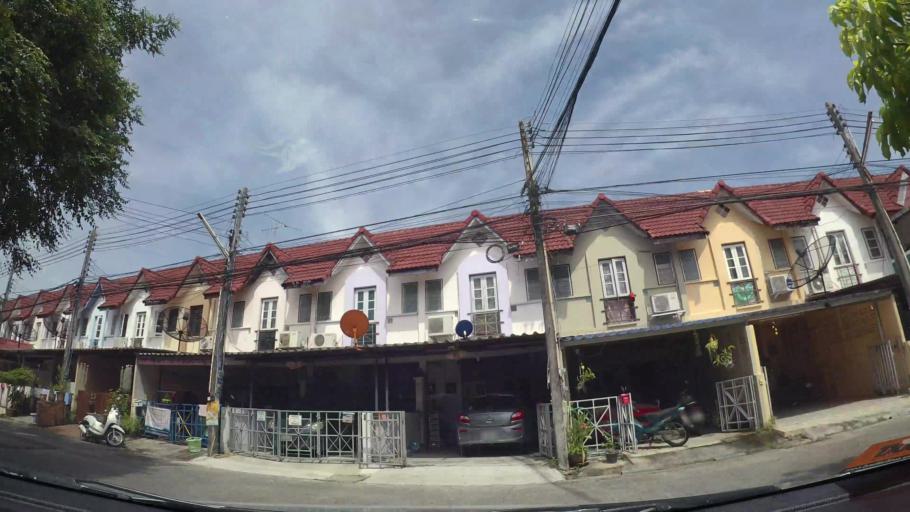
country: TH
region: Chon Buri
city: Chon Buri
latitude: 13.3224
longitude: 100.9489
